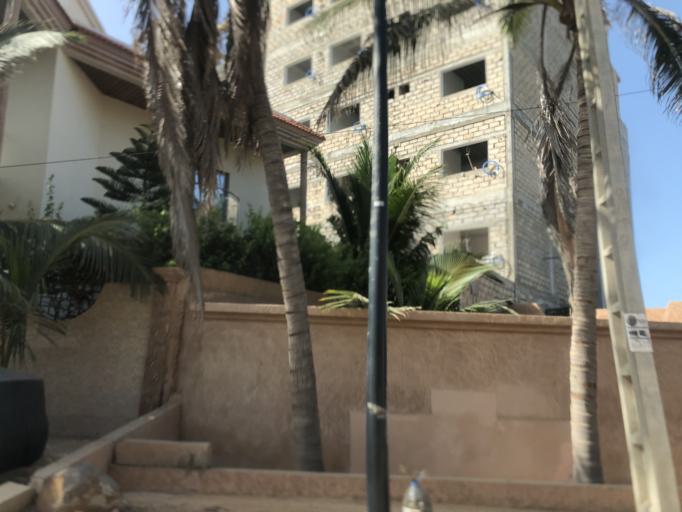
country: SN
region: Dakar
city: Mermoz Boabab
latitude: 14.7565
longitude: -17.4891
